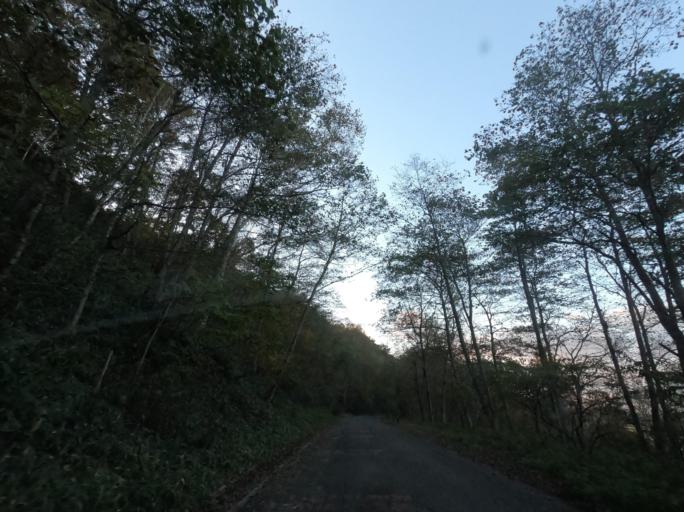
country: JP
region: Hokkaido
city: Kushiro
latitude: 43.1931
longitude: 144.4643
